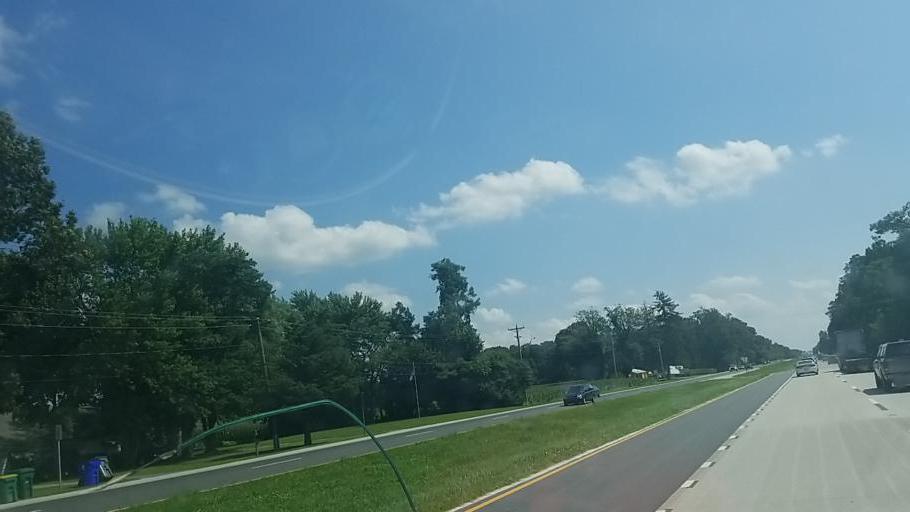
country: US
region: Delaware
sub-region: Sussex County
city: Milford
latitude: 38.8489
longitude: -75.4393
